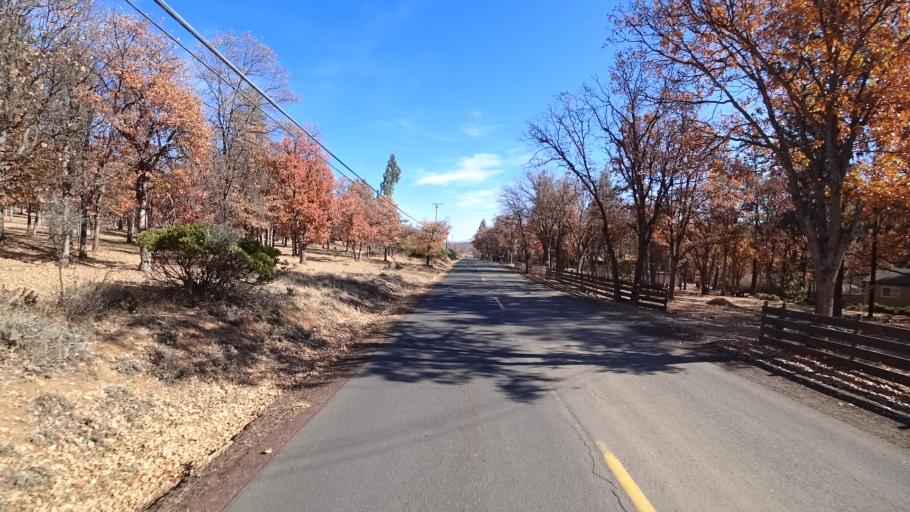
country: US
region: California
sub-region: Siskiyou County
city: Yreka
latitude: 41.7147
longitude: -122.6578
